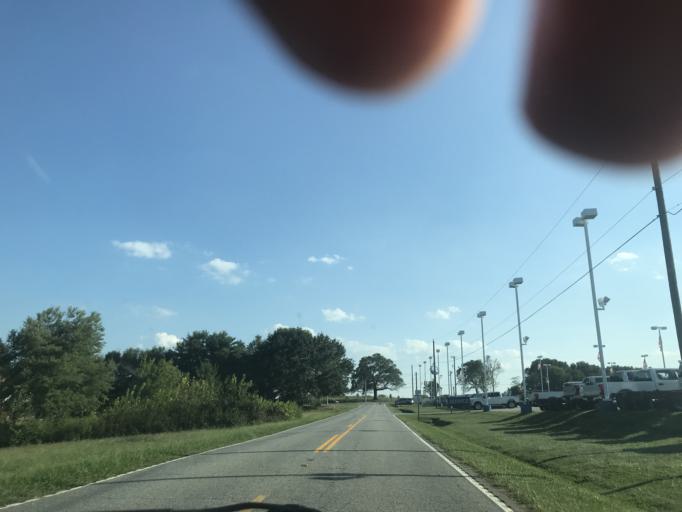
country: US
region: South Carolina
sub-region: Cherokee County
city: Gaffney
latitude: 35.1054
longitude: -81.6809
